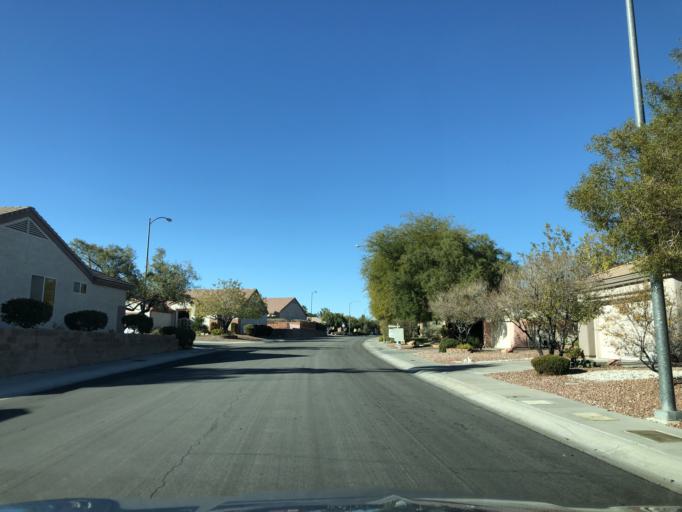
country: US
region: Nevada
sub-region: Clark County
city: Whitney
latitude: 36.0111
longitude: -115.0781
